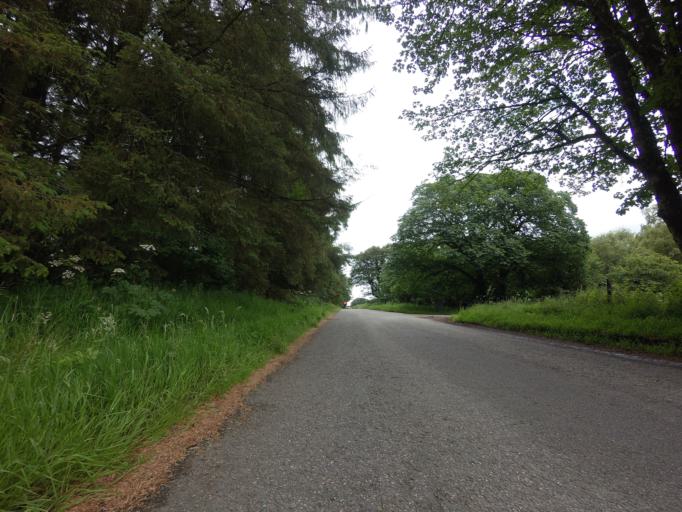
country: GB
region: Scotland
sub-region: Aberdeenshire
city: Mintlaw
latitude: 57.5306
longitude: -2.1513
